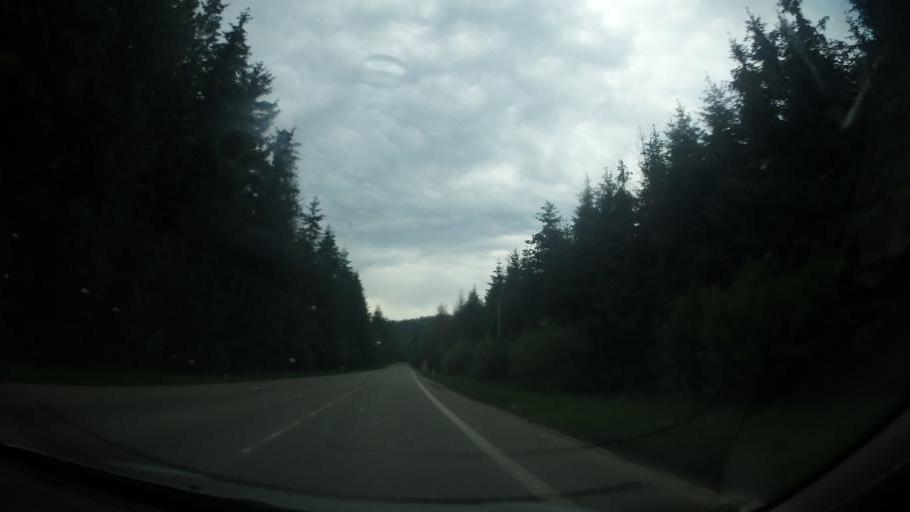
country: CZ
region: South Moravian
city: Olesnice
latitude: 49.4996
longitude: 16.4024
